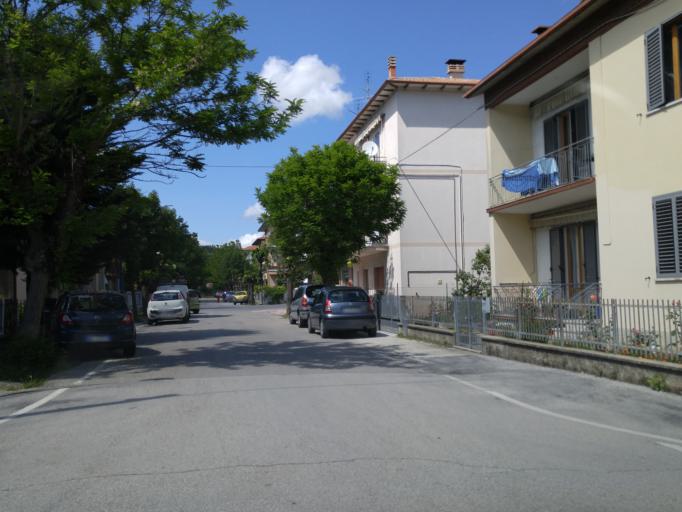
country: IT
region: The Marches
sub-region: Provincia di Pesaro e Urbino
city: Fermignano
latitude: 43.6806
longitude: 12.6464
